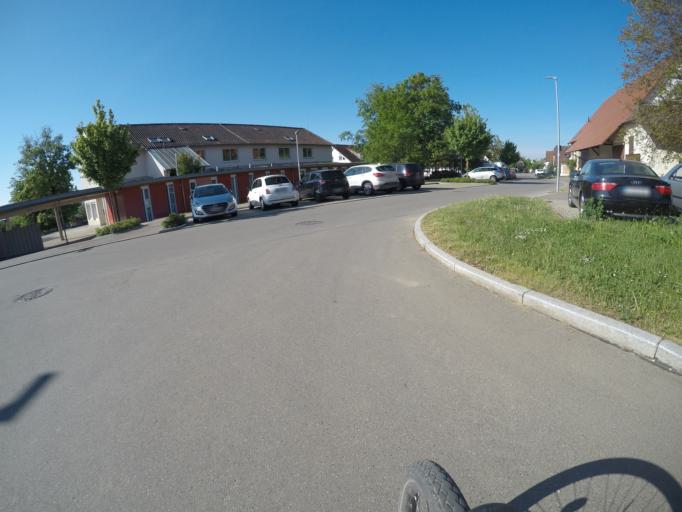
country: DE
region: Baden-Wuerttemberg
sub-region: Regierungsbezirk Stuttgart
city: Schlaitdorf
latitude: 48.6073
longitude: 9.2245
